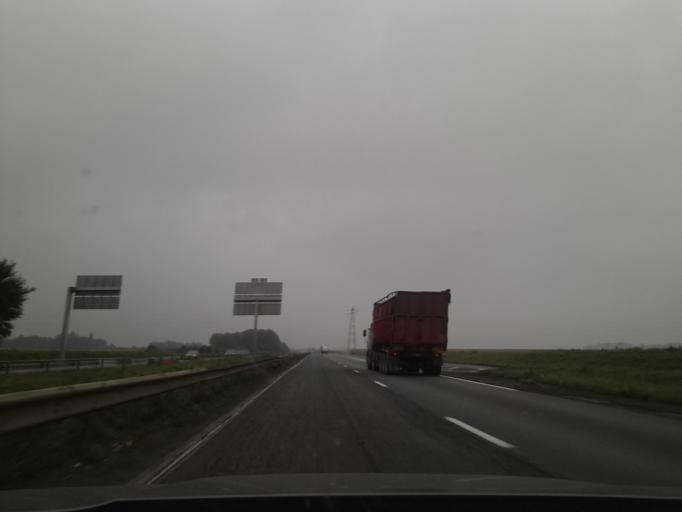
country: FR
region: Nord-Pas-de-Calais
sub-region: Departement du Nord
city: Onnaing
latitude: 50.3668
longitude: 3.5964
